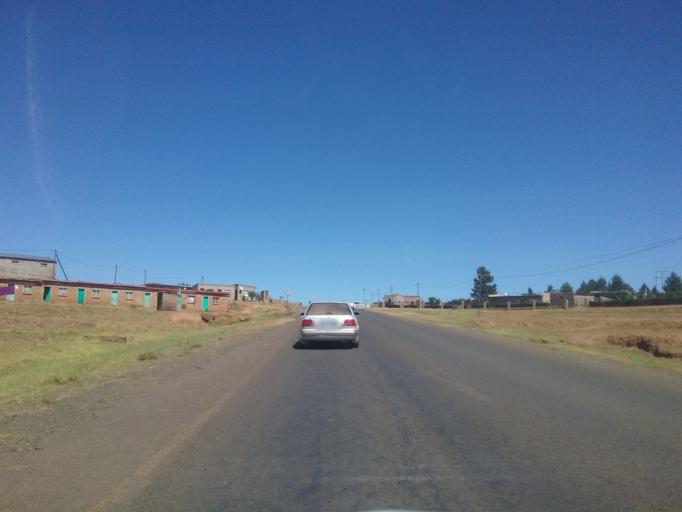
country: LS
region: Quthing
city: Quthing
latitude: -30.3951
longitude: 27.6408
